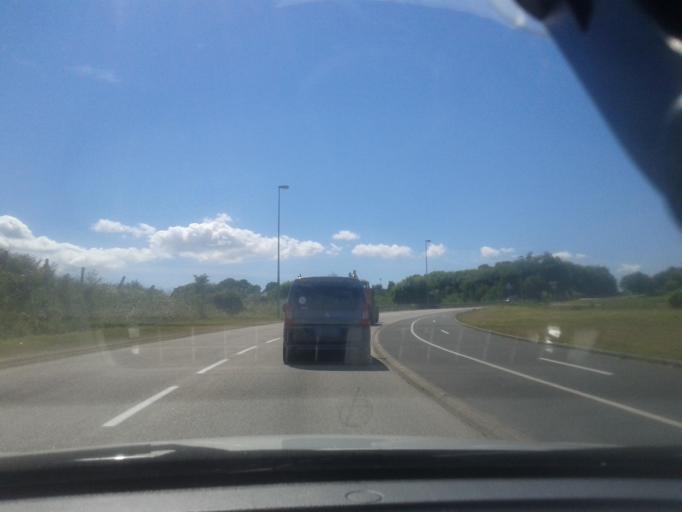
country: FR
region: Lower Normandy
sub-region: Departement de la Manche
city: Equeurdreville-Hainneville
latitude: 49.6351
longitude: -1.6540
